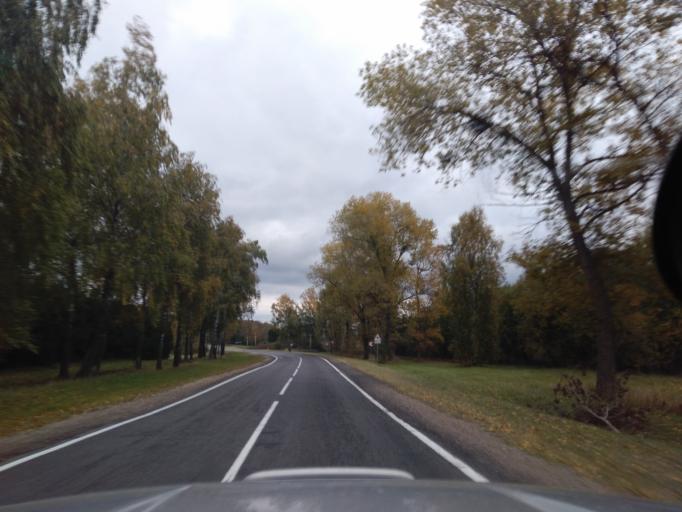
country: BY
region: Minsk
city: Slutsk
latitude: 53.2193
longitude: 27.5274
